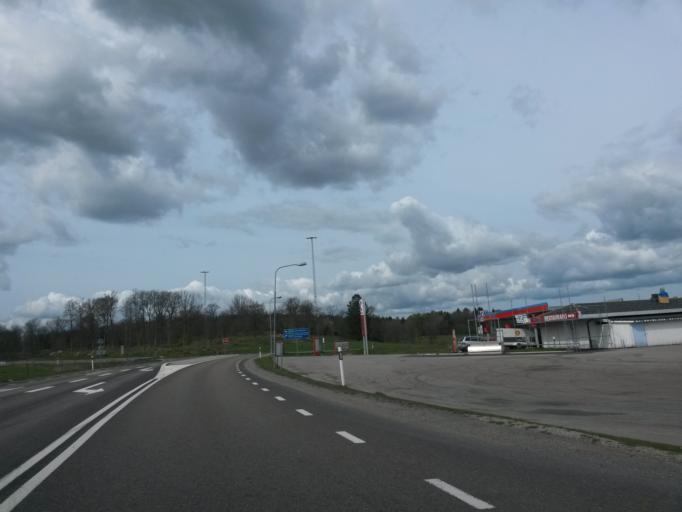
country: SE
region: Vaestra Goetaland
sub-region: Vargarda Kommun
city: Vargarda
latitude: 58.0500
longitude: 12.8160
